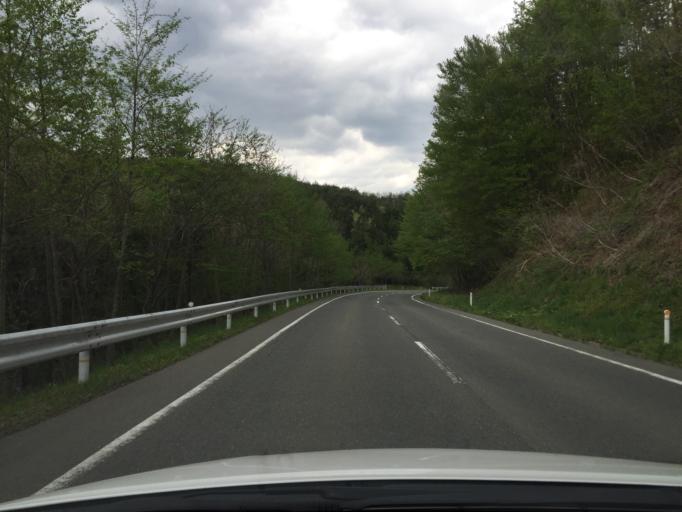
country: JP
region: Miyagi
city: Marumori
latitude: 37.6927
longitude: 140.7953
